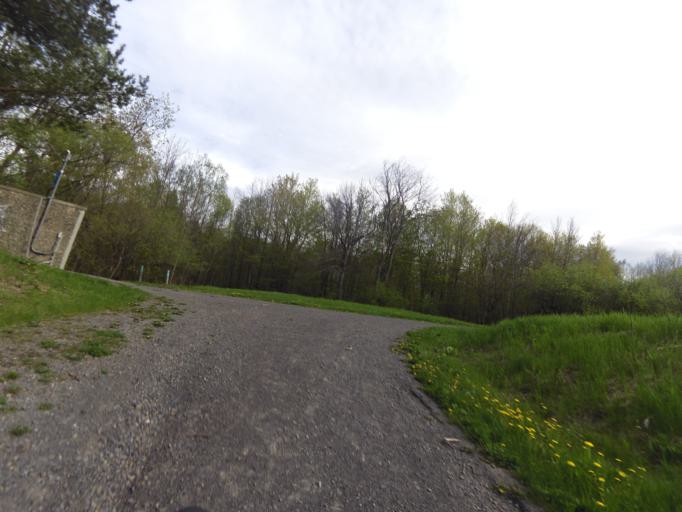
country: CA
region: Ontario
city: Ottawa
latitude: 45.2936
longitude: -75.7135
